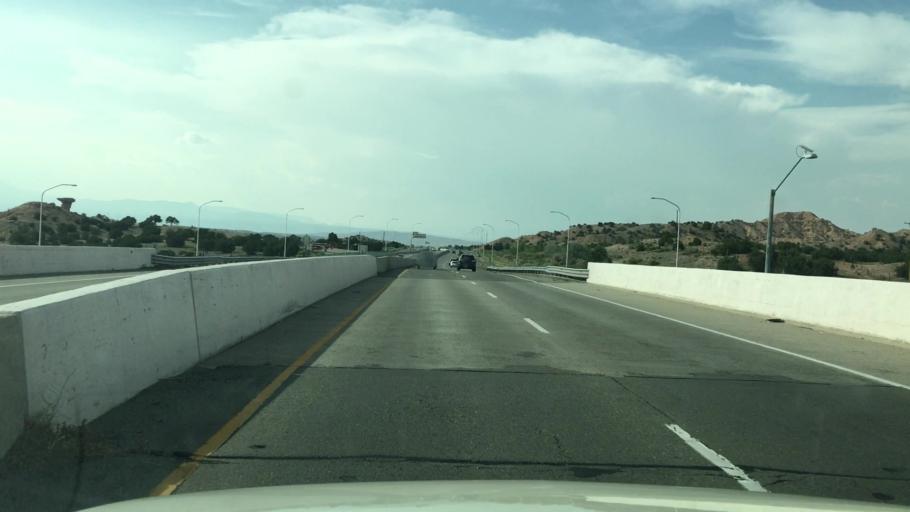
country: US
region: New Mexico
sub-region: Santa Fe County
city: Nambe
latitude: 35.8226
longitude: -105.9762
